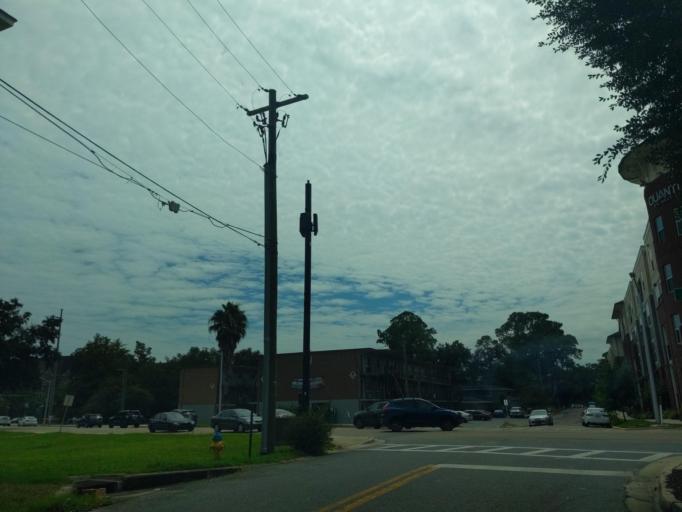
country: US
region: Florida
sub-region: Leon County
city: Tallahassee
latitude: 30.4474
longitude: -84.3078
